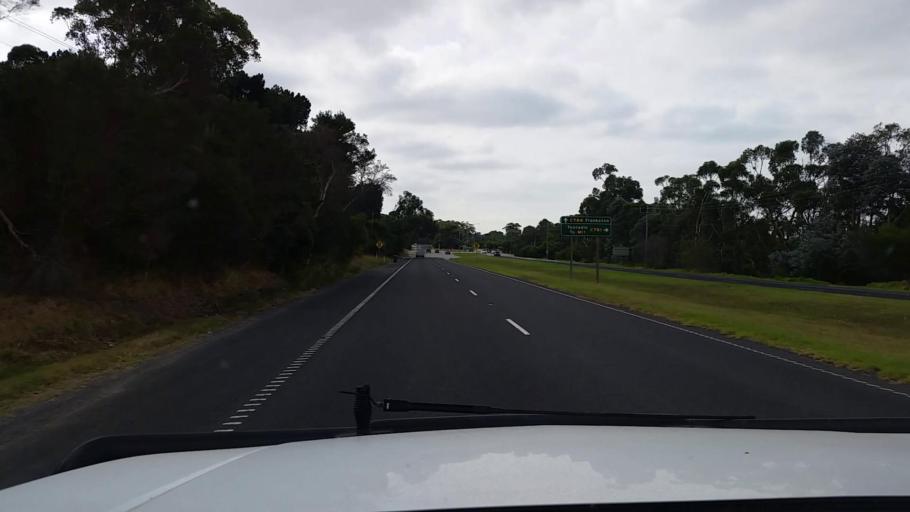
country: AU
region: Victoria
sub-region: Mornington Peninsula
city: Baxter
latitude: -38.1978
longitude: 145.1313
